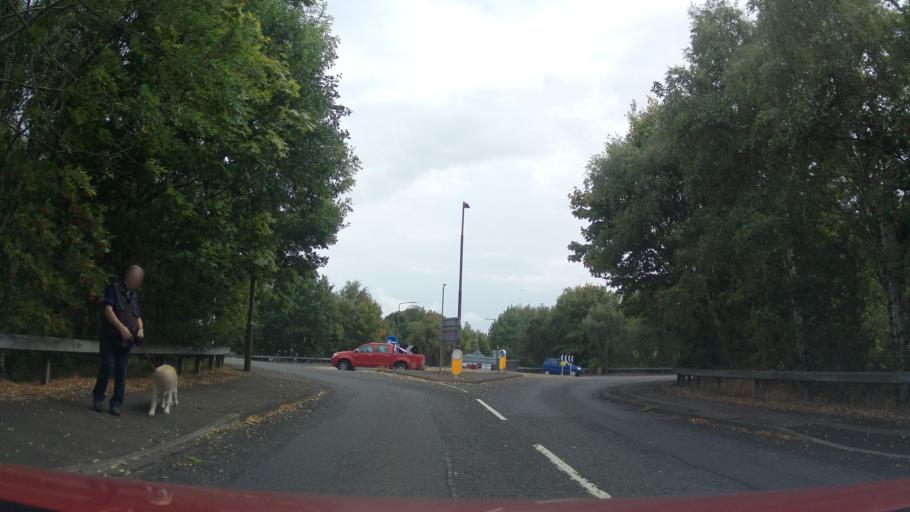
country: GB
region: Scotland
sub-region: East Lothian
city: Tranent
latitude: 55.9586
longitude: -2.9535
